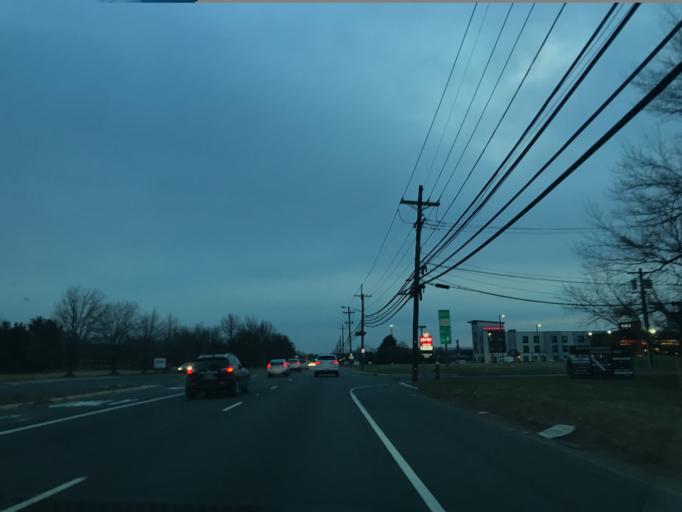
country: US
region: New Jersey
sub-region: Middlesex County
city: Rossmoor
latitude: 40.3437
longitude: -74.4996
